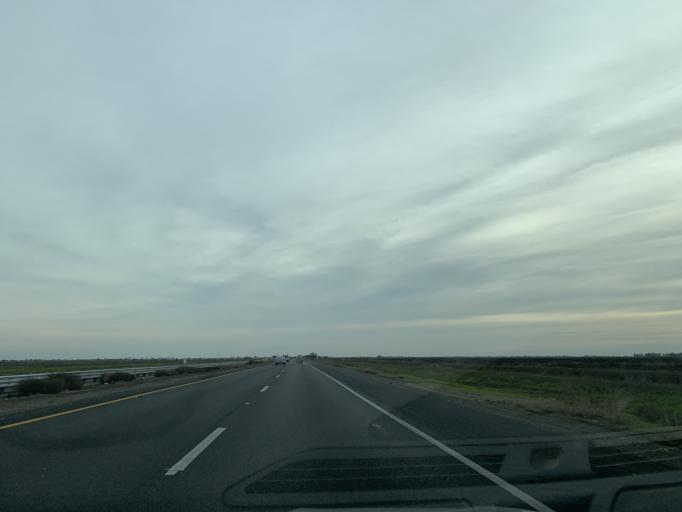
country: US
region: California
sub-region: Sacramento County
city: Elverta
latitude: 38.7036
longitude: -121.5405
